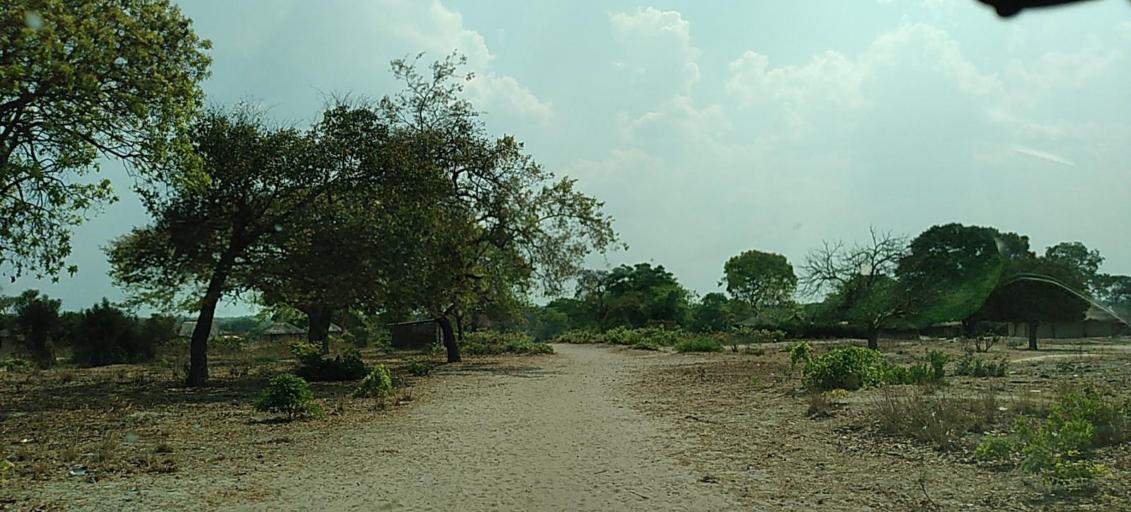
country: ZM
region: North-Western
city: Kabompo
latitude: -13.4465
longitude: 23.6666
